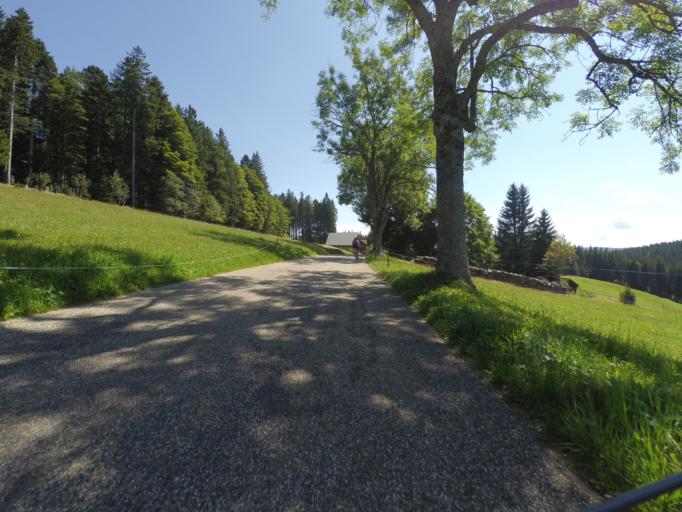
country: DE
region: Baden-Wuerttemberg
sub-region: Freiburg Region
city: Gutenbach
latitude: 48.0622
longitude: 8.1781
